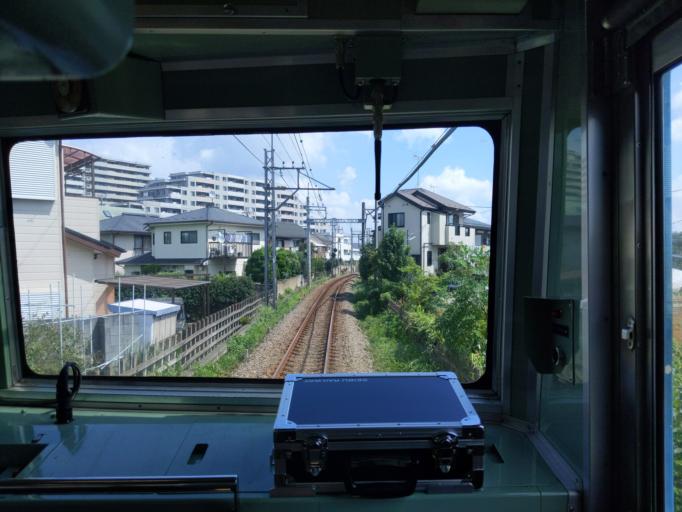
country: JP
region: Tokyo
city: Kamirenjaku
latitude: 35.7008
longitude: 139.5343
